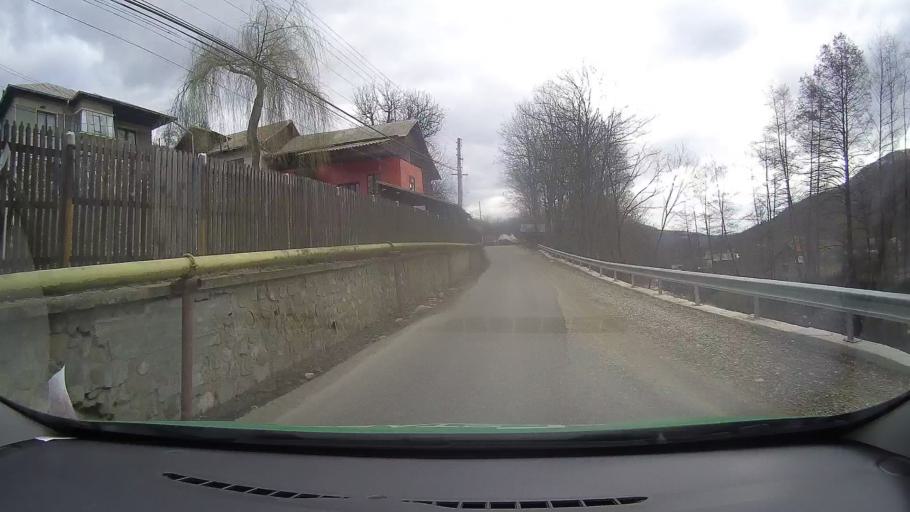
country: RO
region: Dambovita
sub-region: Comuna Visinesti
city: Visinesti
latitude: 45.1036
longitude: 25.5604
